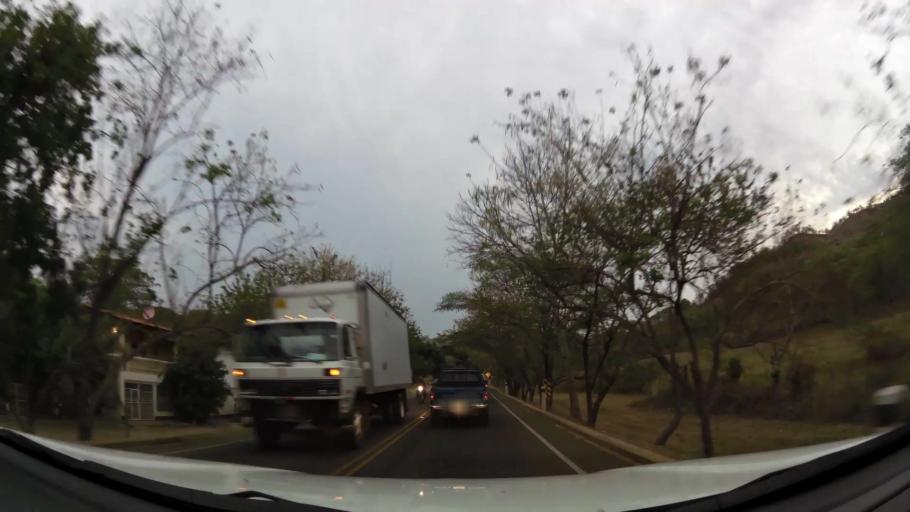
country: NI
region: Esteli
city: Esteli
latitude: 13.0013
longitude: -86.3058
